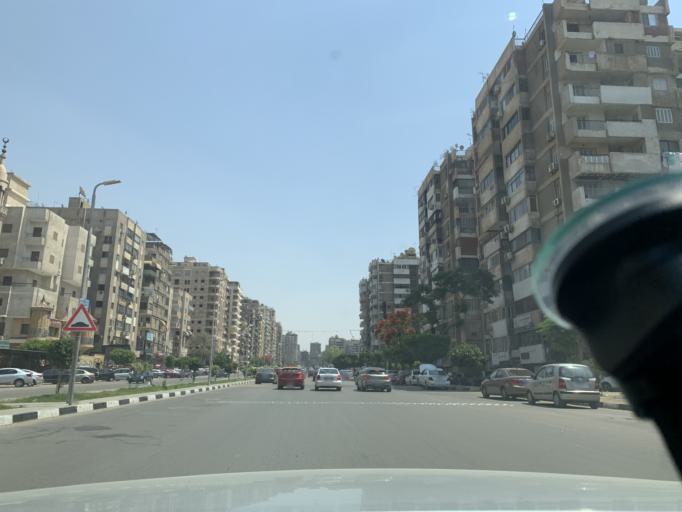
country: EG
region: Muhafazat al Qahirah
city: Cairo
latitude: 30.0672
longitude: 31.3488
